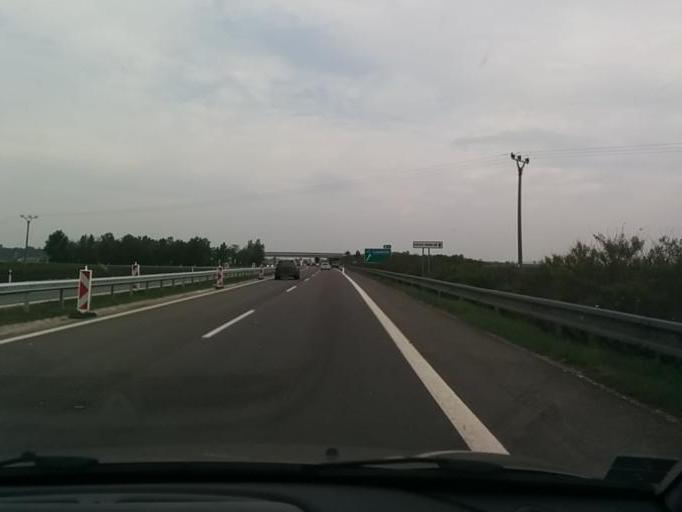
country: SK
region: Trnavsky
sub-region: Okres Galanta
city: Galanta
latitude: 48.2739
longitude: 17.7167
